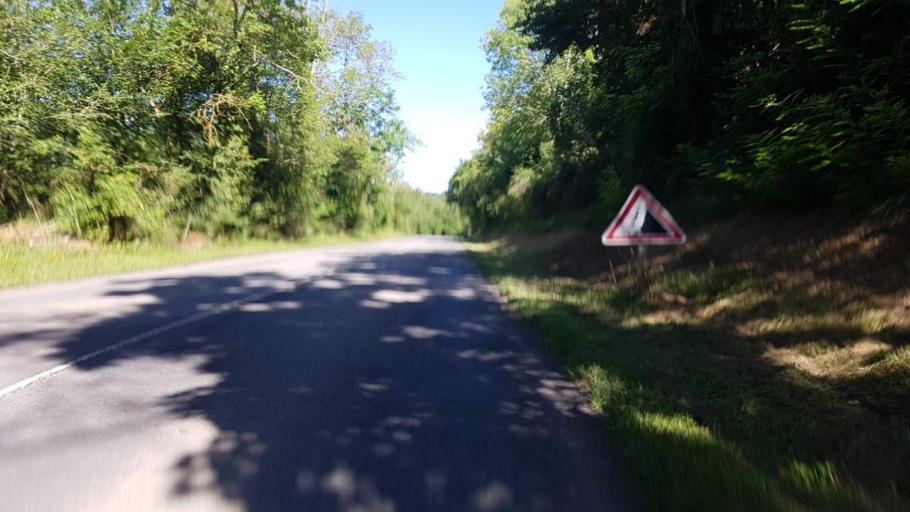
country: FR
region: Picardie
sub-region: Departement de l'Aisne
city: Charly-sur-Marne
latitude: 48.9764
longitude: 3.2502
